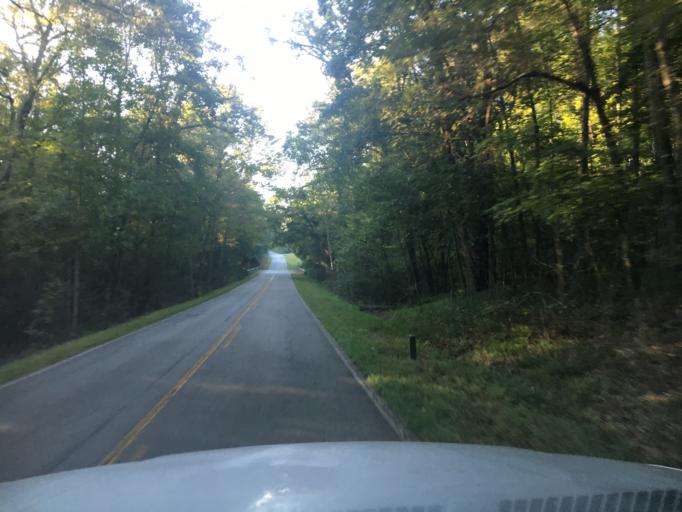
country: US
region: South Carolina
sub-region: Spartanburg County
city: Woodruff
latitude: 34.7697
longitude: -81.9654
